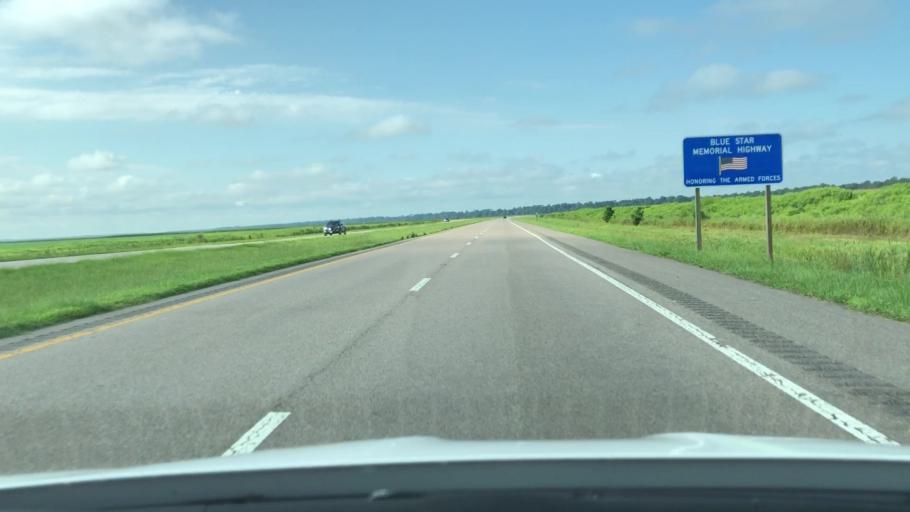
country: US
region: North Carolina
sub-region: Currituck County
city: Moyock
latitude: 36.5925
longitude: -76.3789
